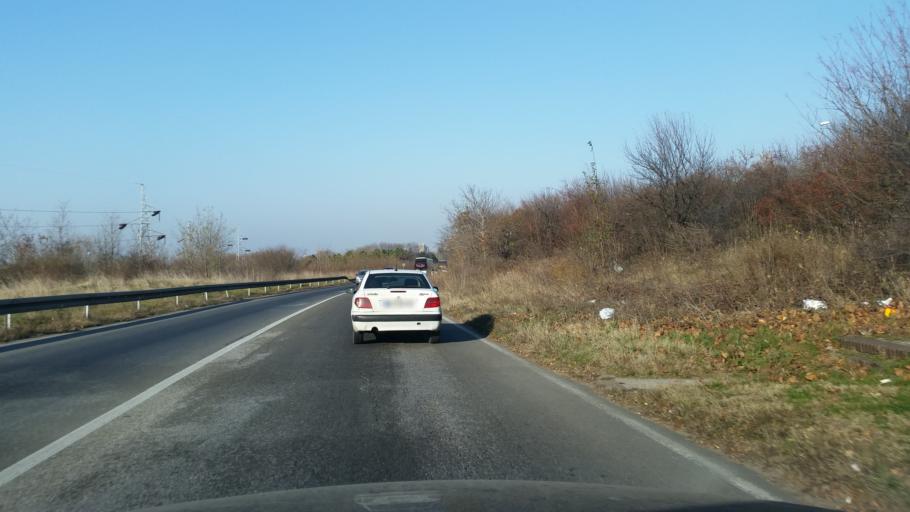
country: RS
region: Central Serbia
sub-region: Belgrade
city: Rakovica
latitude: 44.7435
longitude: 20.4117
